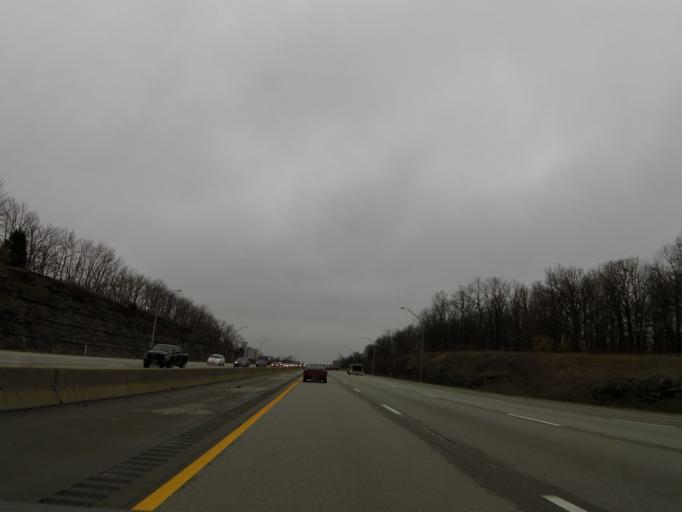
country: US
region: Kentucky
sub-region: Scott County
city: Georgetown
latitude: 38.2727
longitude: -84.5564
